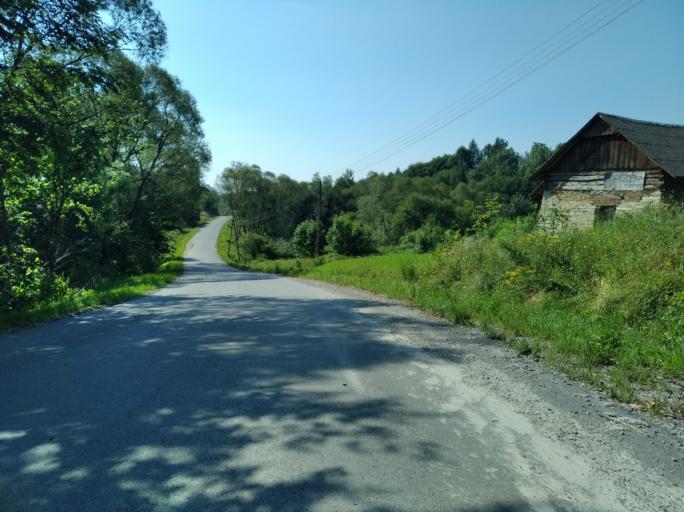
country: PL
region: Subcarpathian Voivodeship
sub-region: Powiat brzozowski
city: Wesola
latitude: 49.8317
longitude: 22.1466
